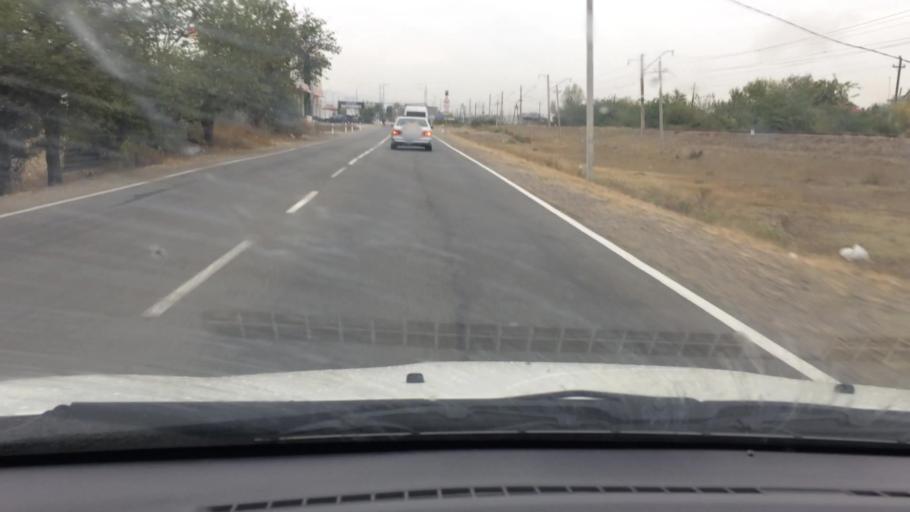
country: GE
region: Kvemo Kartli
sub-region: Marneuli
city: Marneuli
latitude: 41.4573
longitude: 44.8112
